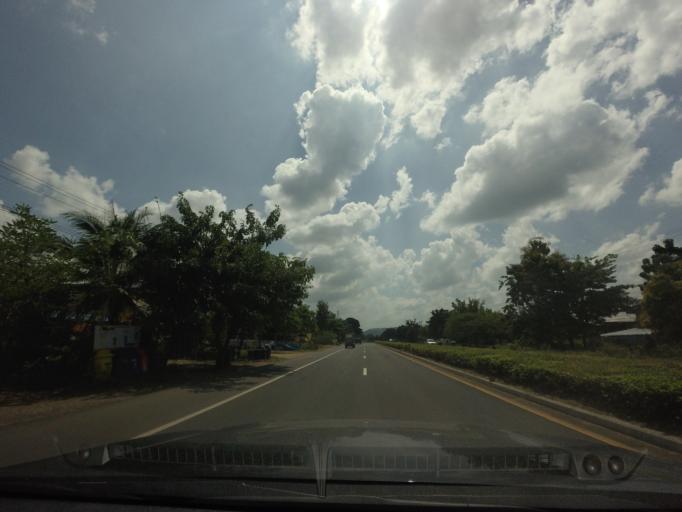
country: TH
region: Phetchabun
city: Phetchabun
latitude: 16.2749
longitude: 101.0590
